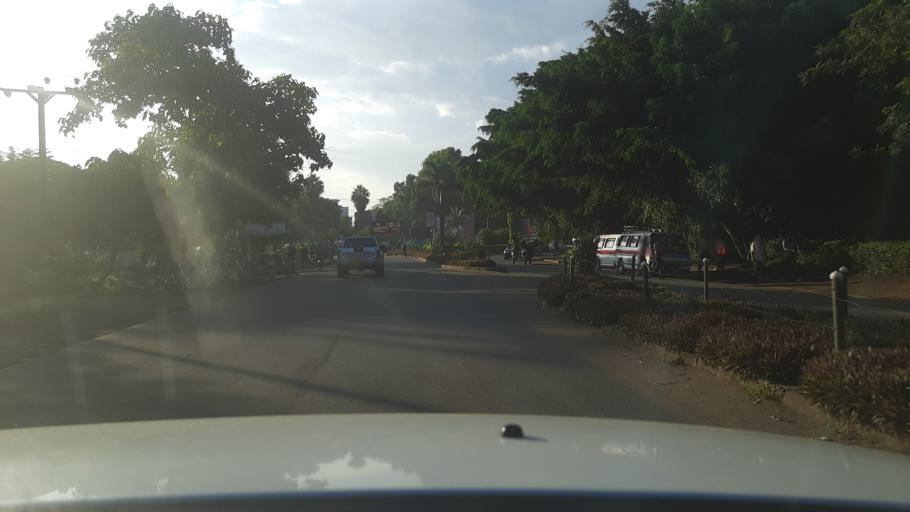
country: TZ
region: Arusha
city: Arusha
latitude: -3.3779
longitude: 36.7039
